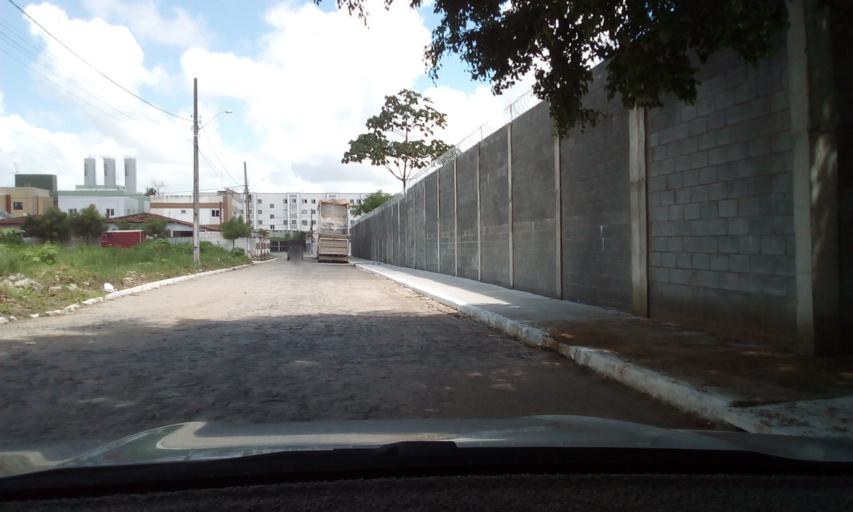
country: BR
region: Paraiba
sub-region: Bayeux
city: Bayeux
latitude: -7.1690
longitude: -34.8916
